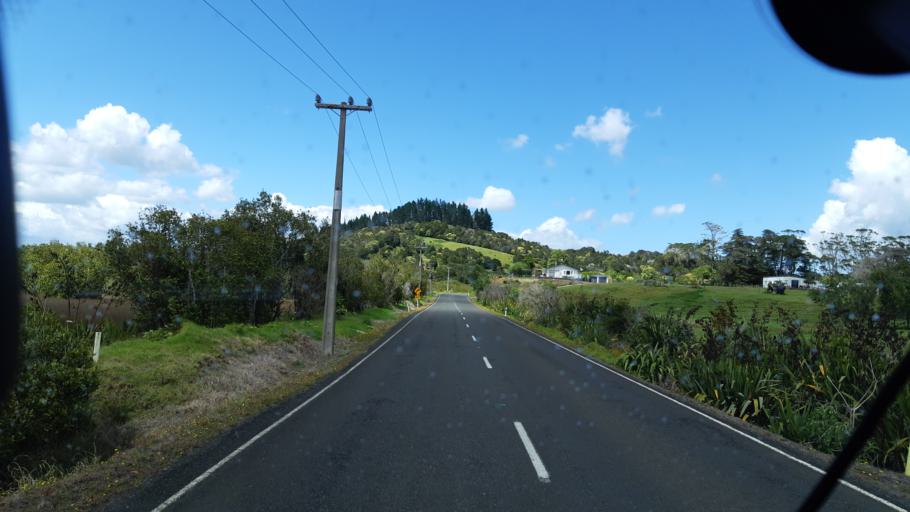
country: NZ
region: Northland
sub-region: Far North District
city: Taipa
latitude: -35.2723
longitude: 173.5220
